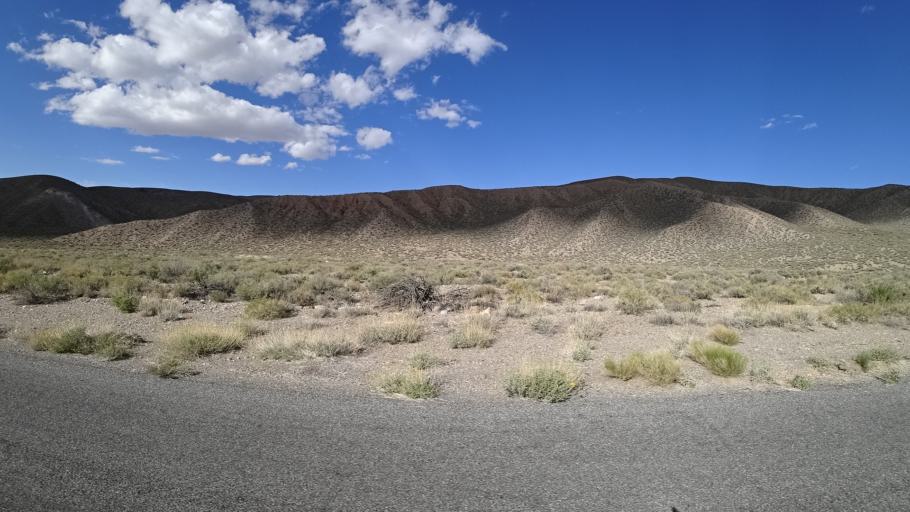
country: US
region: Nevada
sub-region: Nye County
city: Beatty
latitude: 36.4022
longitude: -117.1672
